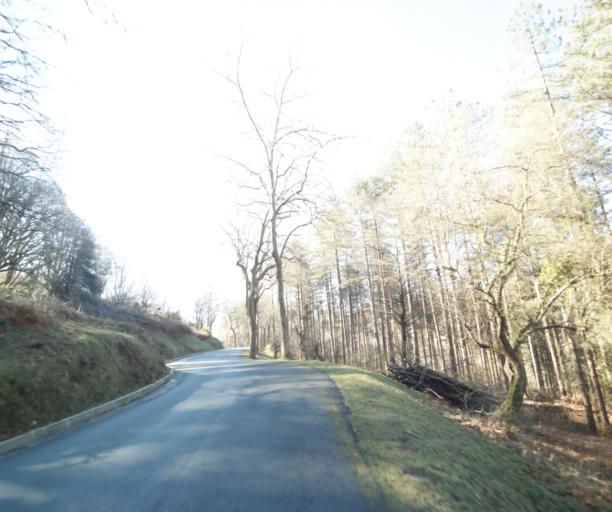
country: ES
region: Navarre
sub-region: Provincia de Navarra
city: Bera
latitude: 43.3145
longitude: -1.6849
